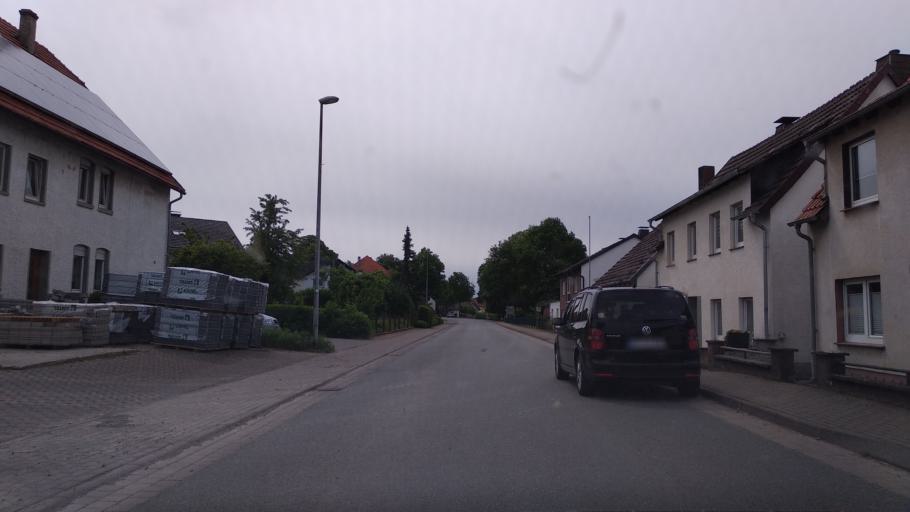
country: DE
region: North Rhine-Westphalia
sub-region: Regierungsbezirk Detmold
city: Willebadessen
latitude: 51.6021
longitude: 9.1280
